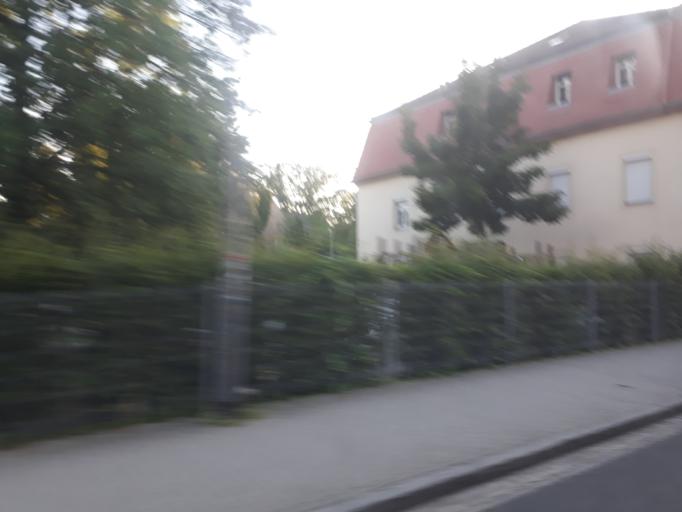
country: DE
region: Saxony
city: Radeberg
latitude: 51.0591
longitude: 13.8857
